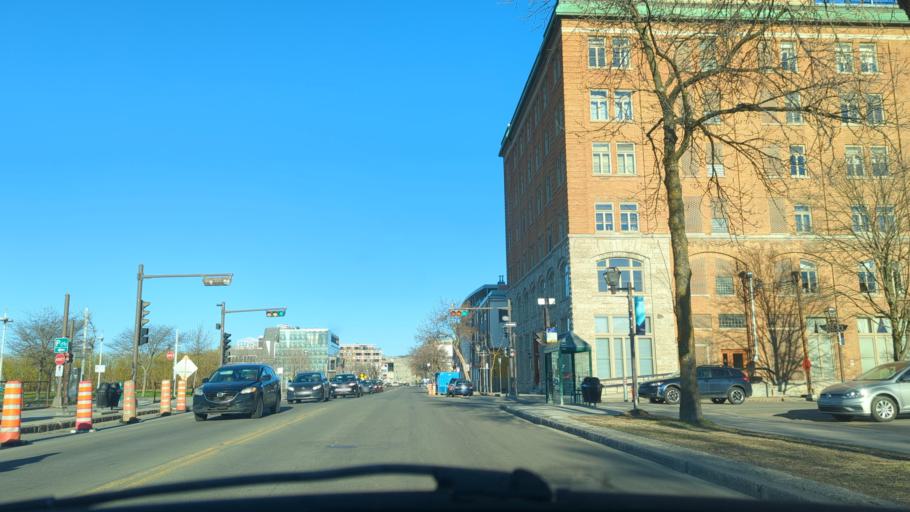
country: CA
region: Quebec
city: Quebec
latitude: 46.8174
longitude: -71.2088
